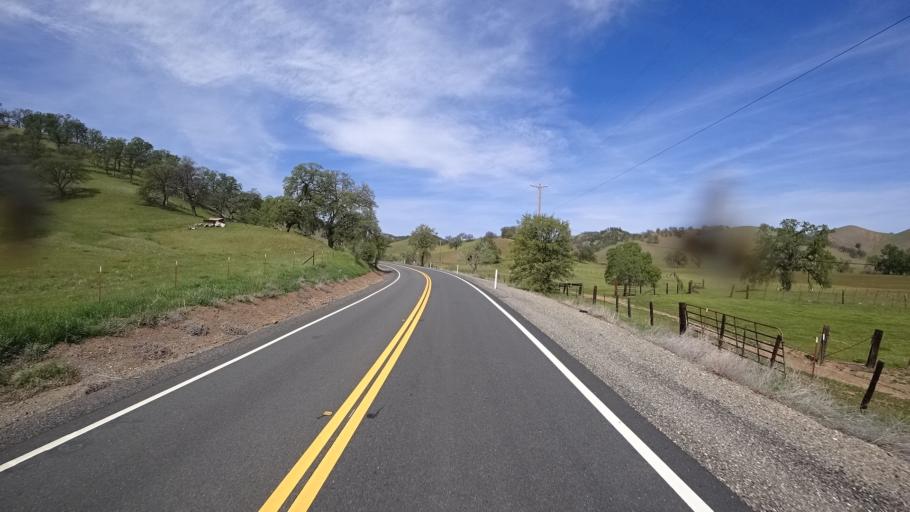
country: US
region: California
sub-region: Glenn County
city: Willows
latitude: 39.5938
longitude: -122.4616
